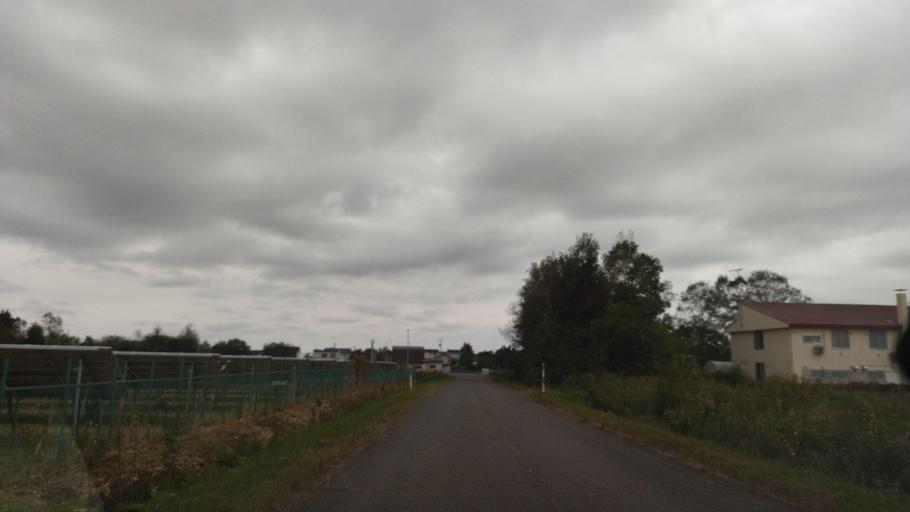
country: JP
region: Hokkaido
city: Otofuke
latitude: 43.2412
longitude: 143.2952
